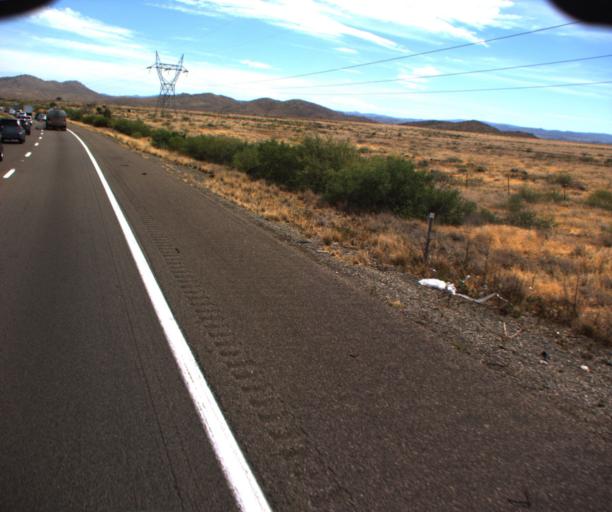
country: US
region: Arizona
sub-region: Yavapai County
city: Cordes Lakes
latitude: 34.2158
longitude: -112.1117
